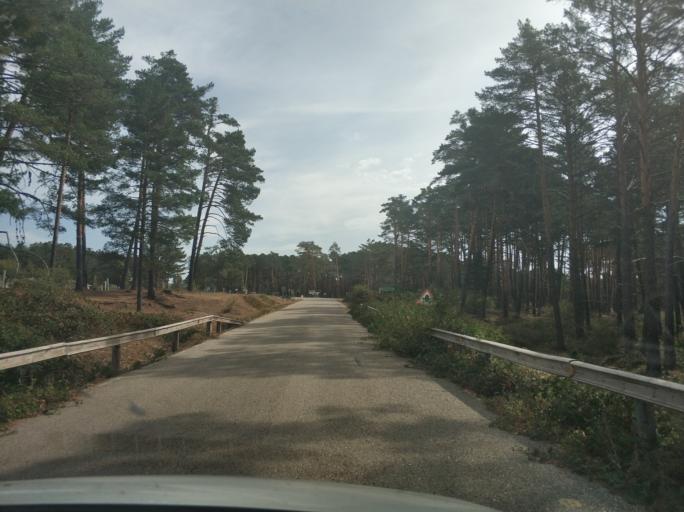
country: ES
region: Castille and Leon
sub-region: Provincia de Soria
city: Navaleno
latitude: 41.8560
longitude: -2.9481
